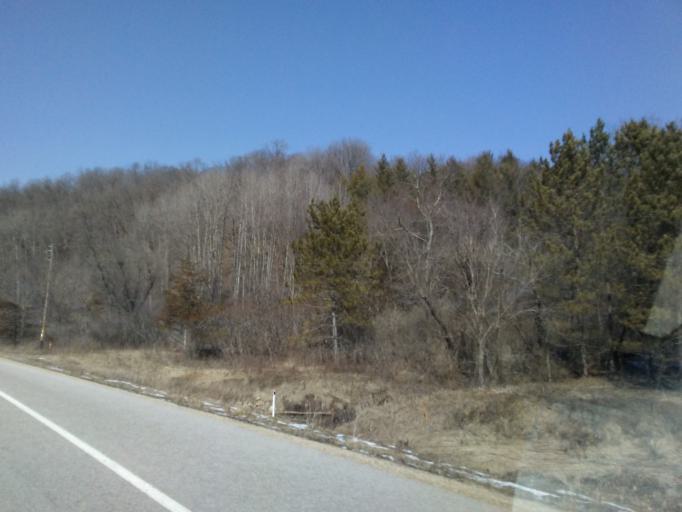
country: US
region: Wisconsin
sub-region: Vernon County
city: Viroqua
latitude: 43.4490
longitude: -90.7070
